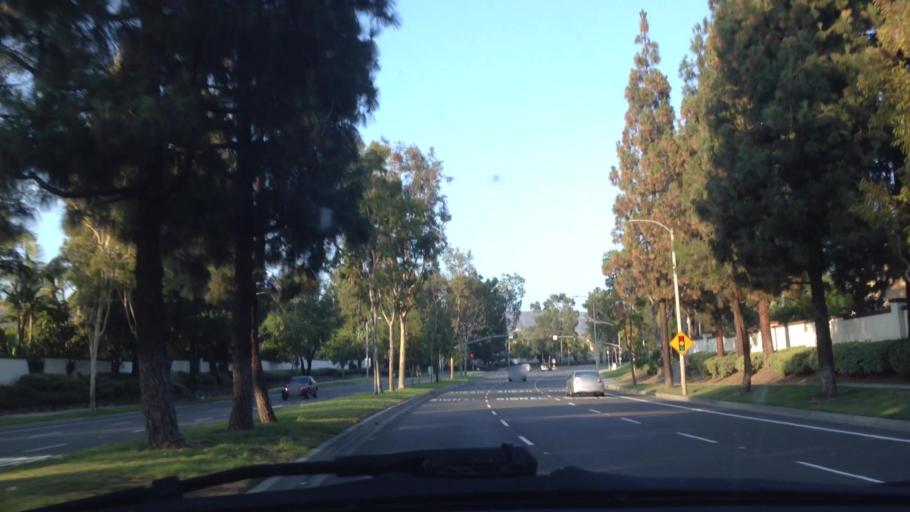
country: US
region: California
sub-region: Orange County
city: North Tustin
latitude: 33.7430
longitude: -117.7882
